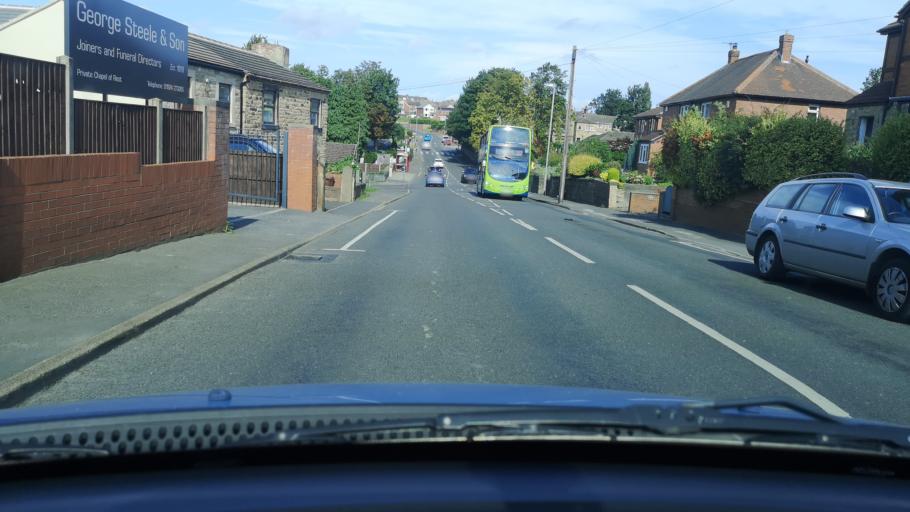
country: GB
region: England
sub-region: City and Borough of Wakefield
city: Ossett
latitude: 53.6739
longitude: -1.5775
